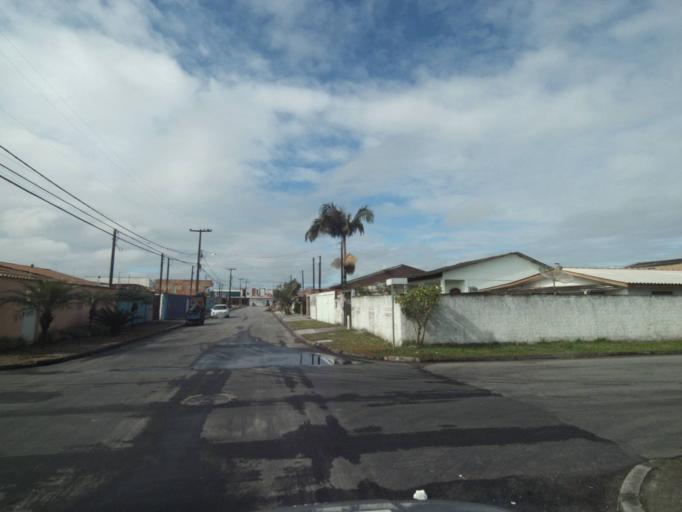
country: BR
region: Parana
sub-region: Paranagua
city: Paranagua
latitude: -25.5629
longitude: -48.5670
